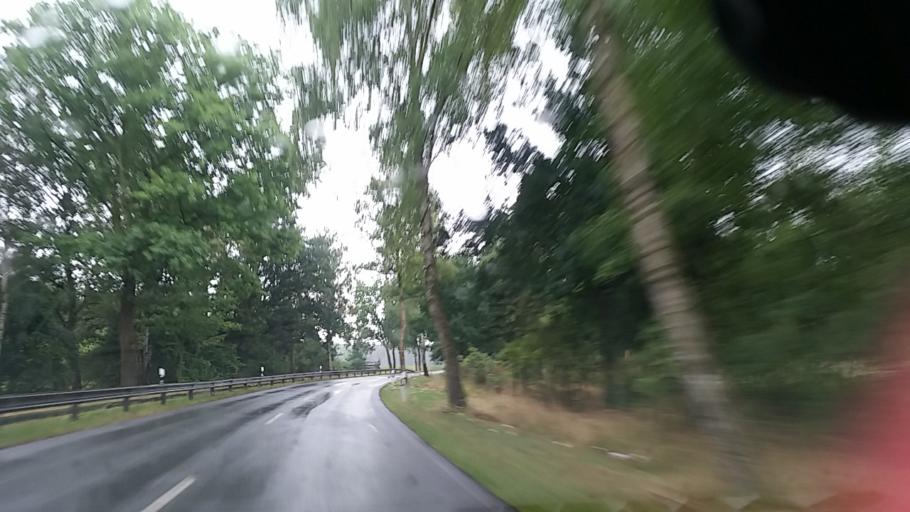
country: DE
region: Lower Saxony
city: Bokensdorf
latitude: 52.5394
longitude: 10.7176
